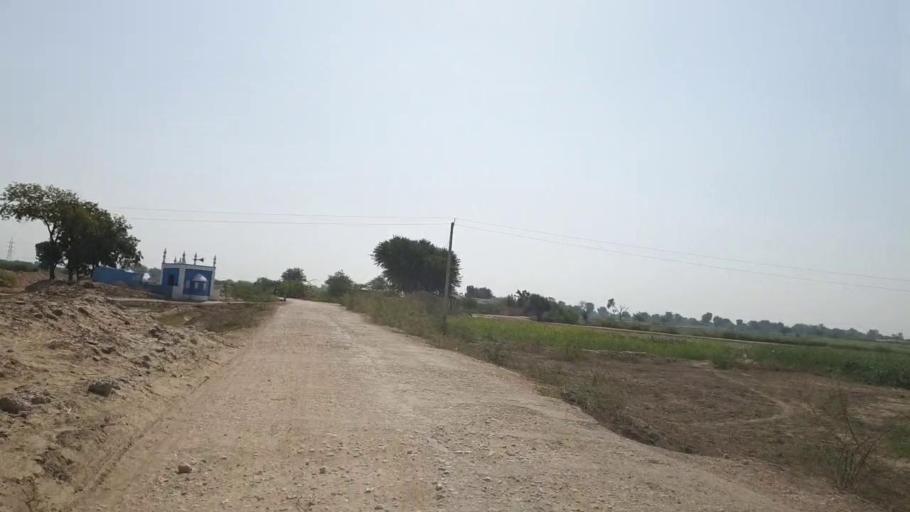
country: PK
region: Sindh
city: Naukot
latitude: 25.0020
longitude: 69.4659
